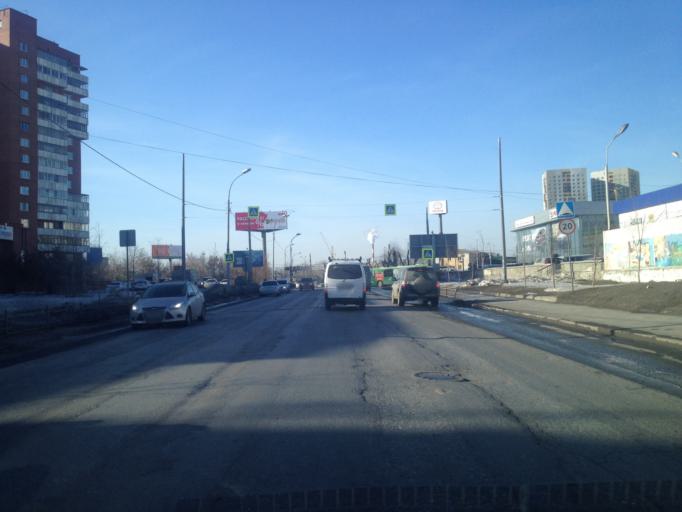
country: RU
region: Sverdlovsk
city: Yekaterinburg
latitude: 56.8557
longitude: 60.6171
